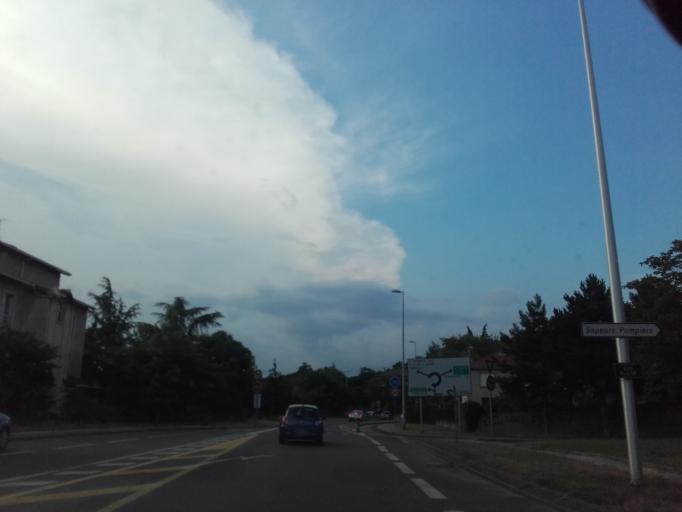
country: FR
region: Rhone-Alpes
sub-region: Departement de l'Isere
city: Le Peage-de-Roussillon
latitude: 45.3763
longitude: 4.7993
